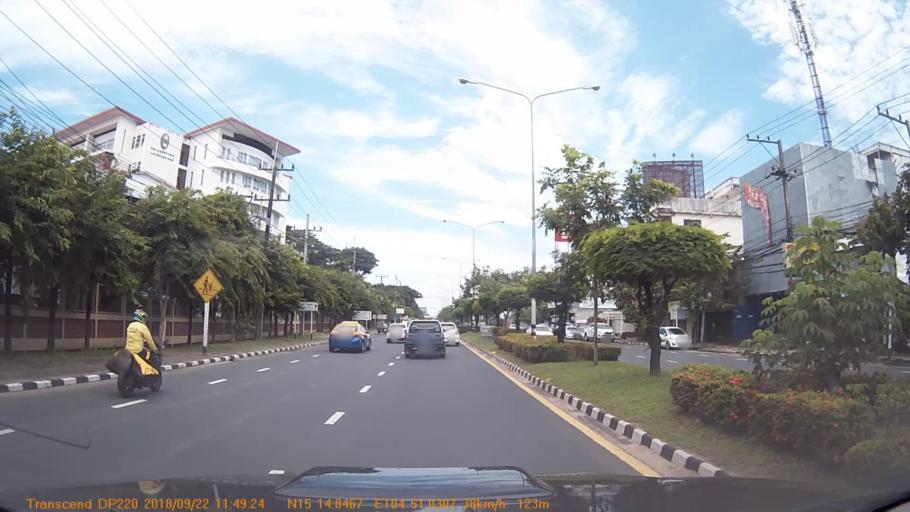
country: TH
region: Changwat Ubon Ratchathani
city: Ubon Ratchathani
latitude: 15.2474
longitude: 104.8505
